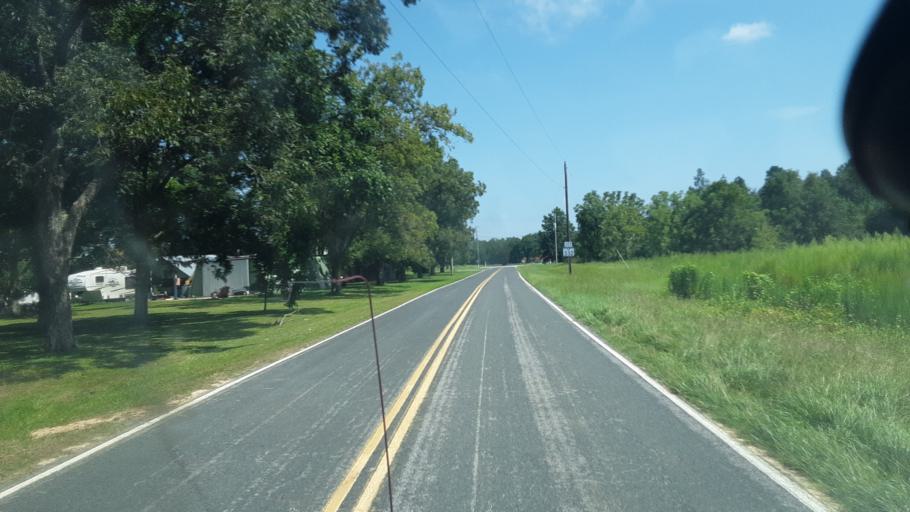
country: US
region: South Carolina
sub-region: Bamberg County
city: Bamberg
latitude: 33.3744
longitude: -81.0130
